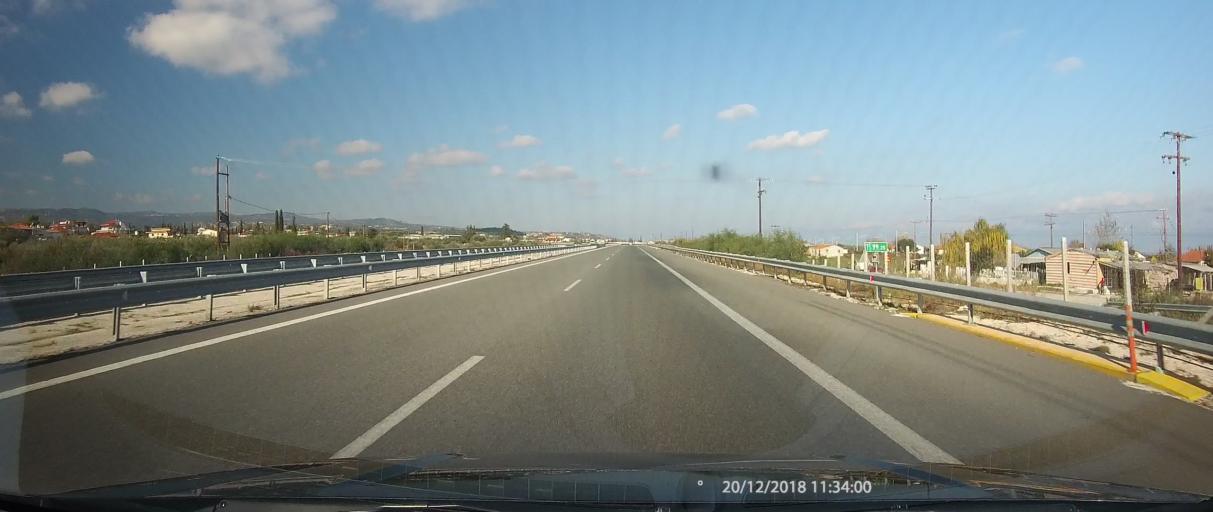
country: GR
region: Peloponnese
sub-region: Nomos Korinthias
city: Velo
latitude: 37.9537
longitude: 22.7537
